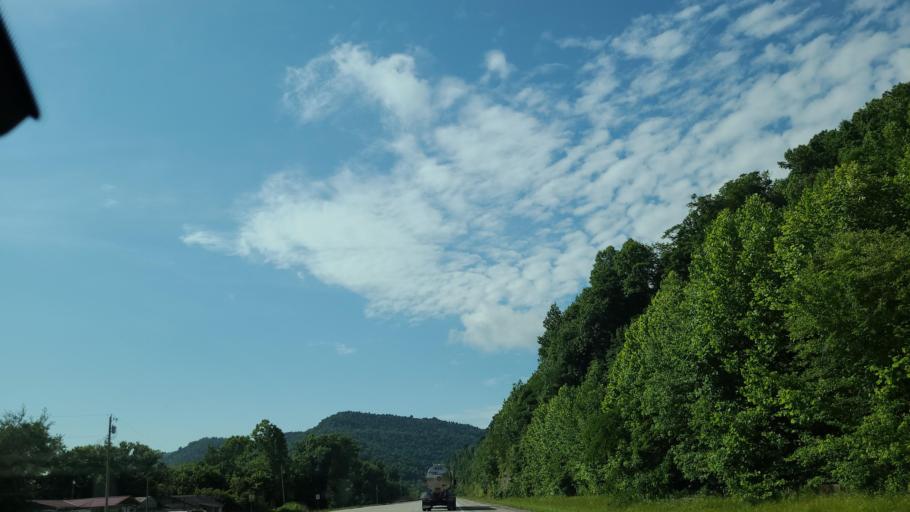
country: US
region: Kentucky
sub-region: Bell County
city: Pineville
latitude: 36.7831
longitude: -83.7400
